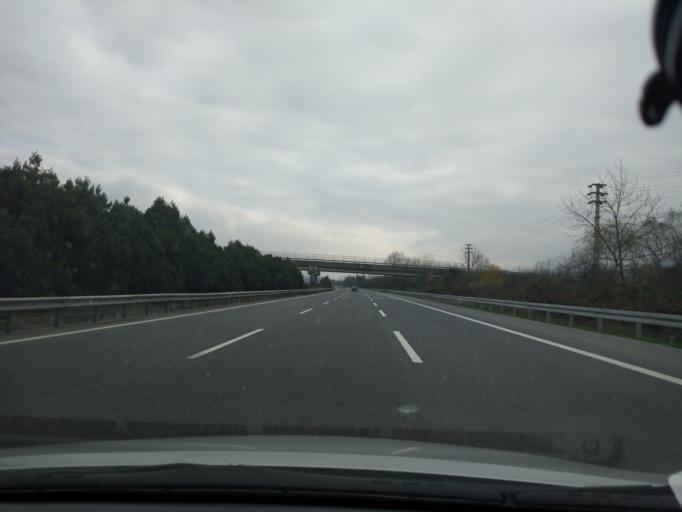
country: TR
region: Duzce
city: Duzce
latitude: 40.7915
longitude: 31.2132
